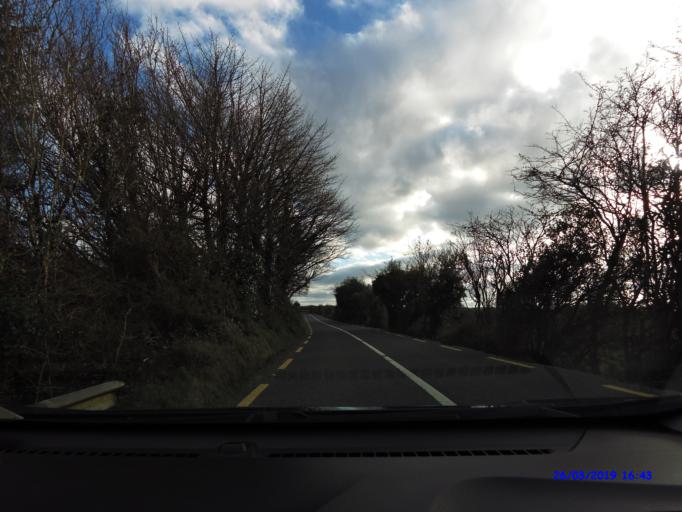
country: IE
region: Connaught
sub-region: Maigh Eo
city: Ballyhaunis
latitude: 53.8599
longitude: -8.7655
